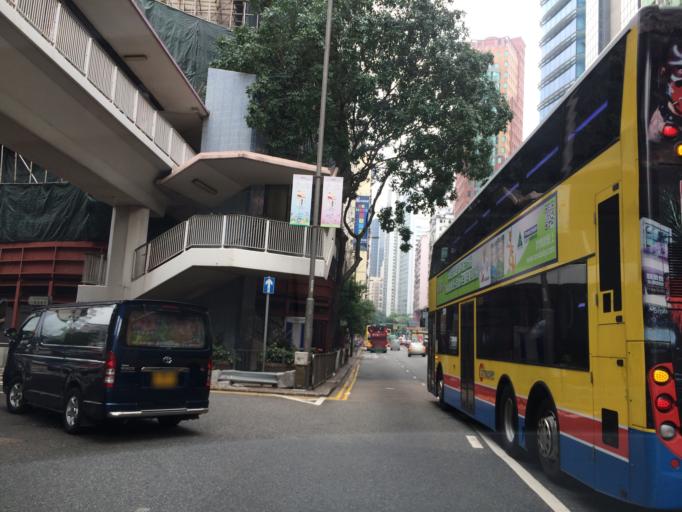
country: HK
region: Wanchai
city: Wan Chai
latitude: 22.2777
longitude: 114.1682
